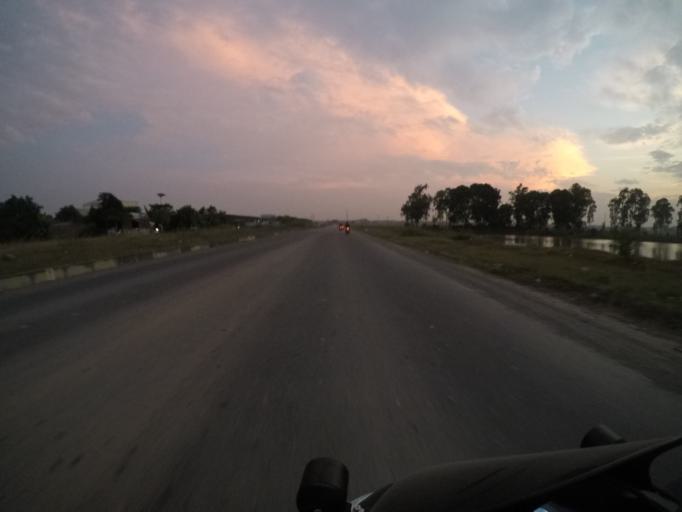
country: VN
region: Vinh Phuc
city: Phuc Yen
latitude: 21.2505
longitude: 105.7214
